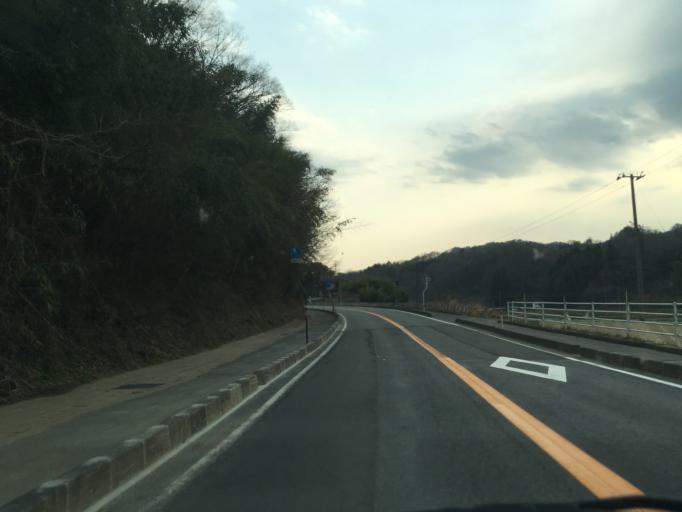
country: JP
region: Fukushima
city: Hobaramachi
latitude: 37.7055
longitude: 140.6083
